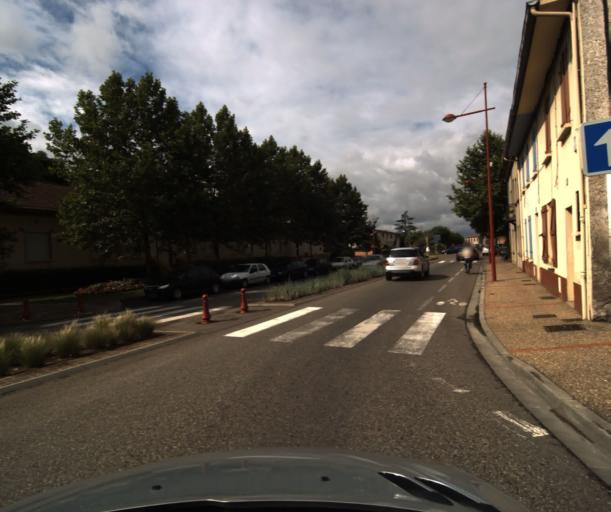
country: FR
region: Midi-Pyrenees
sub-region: Departement du Tarn-et-Garonne
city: Castelsarrasin
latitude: 44.0418
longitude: 1.1050
